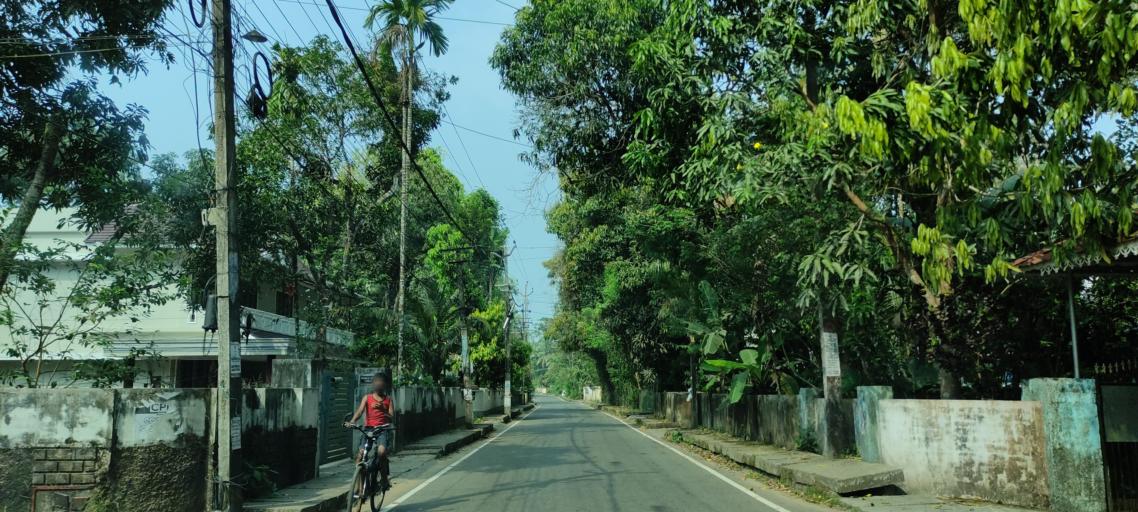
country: IN
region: Kerala
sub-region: Kottayam
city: Vaikam
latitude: 9.7467
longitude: 76.4019
